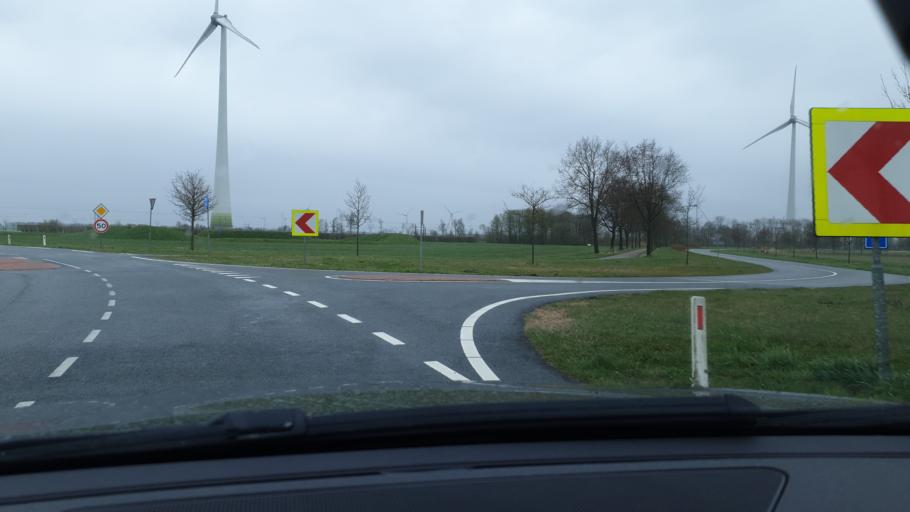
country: NL
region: Flevoland
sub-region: Gemeente Lelystad
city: Lelystad
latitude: 52.5514
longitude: 5.5667
